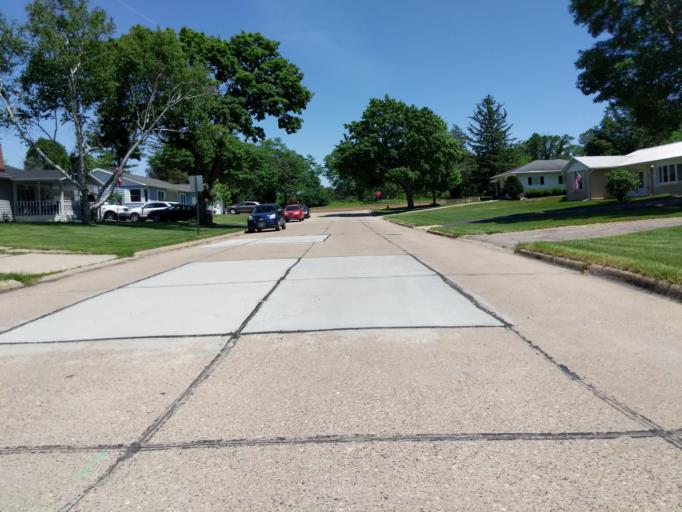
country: US
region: Iowa
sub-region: Linn County
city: Cedar Rapids
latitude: 42.0215
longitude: -91.6397
